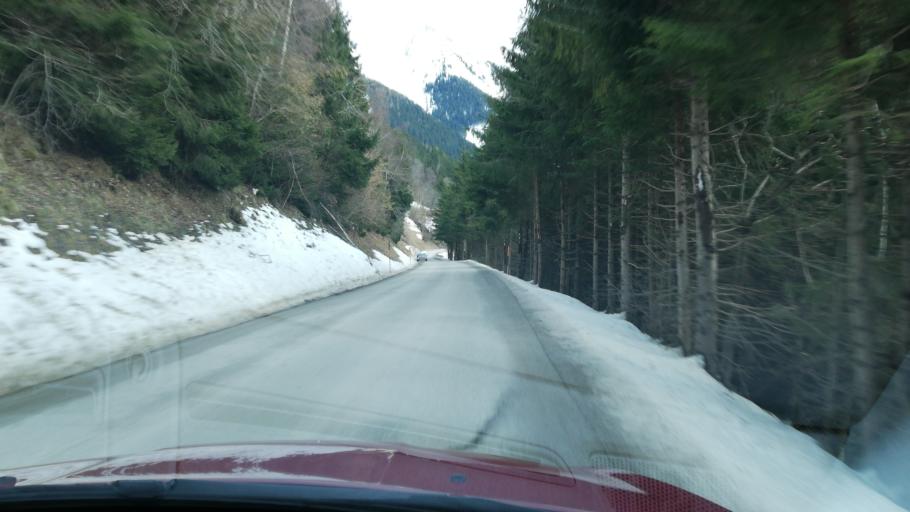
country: AT
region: Styria
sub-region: Politischer Bezirk Liezen
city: Donnersbach
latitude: 47.4381
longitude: 14.1453
